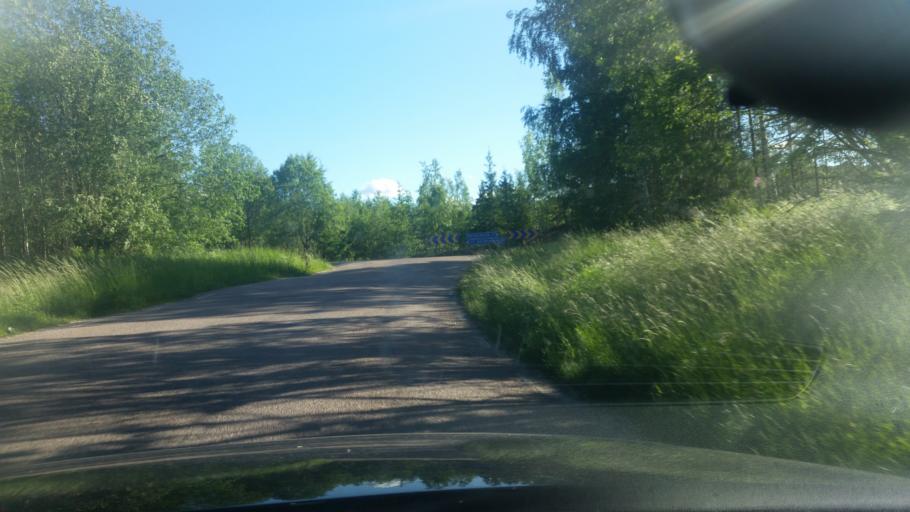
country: SE
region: Soedermanland
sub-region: Katrineholms Kommun
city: Katrineholm
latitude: 59.0881
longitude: 16.0736
